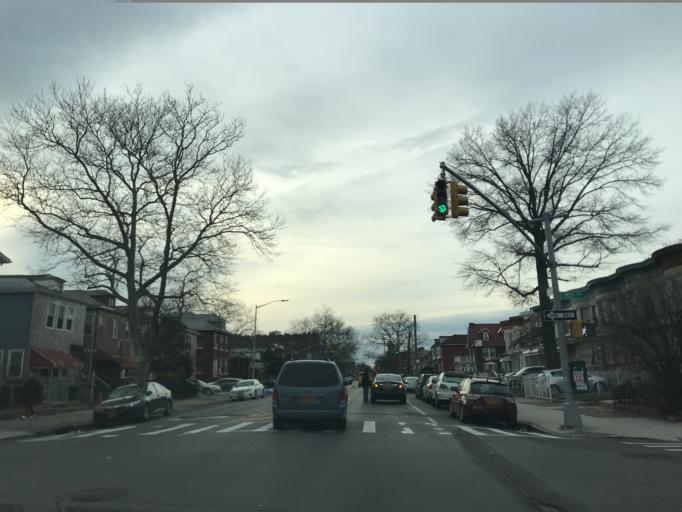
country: US
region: New York
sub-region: Kings County
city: Brooklyn
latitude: 40.6535
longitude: -73.9361
